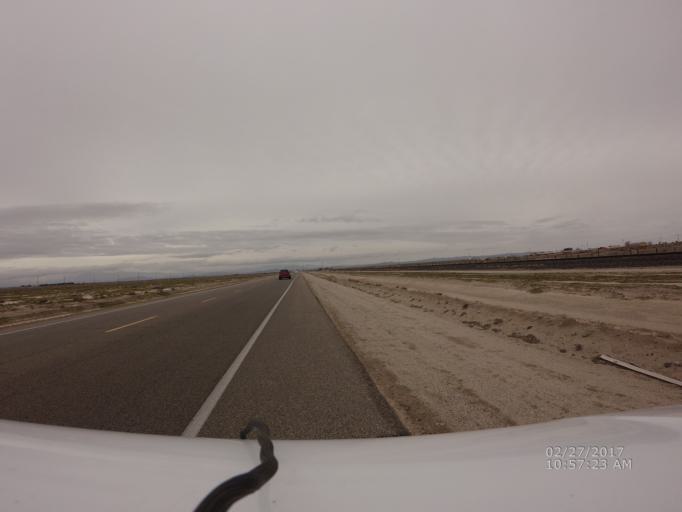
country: US
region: California
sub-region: Los Angeles County
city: Lancaster
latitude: 34.7445
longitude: -118.1440
